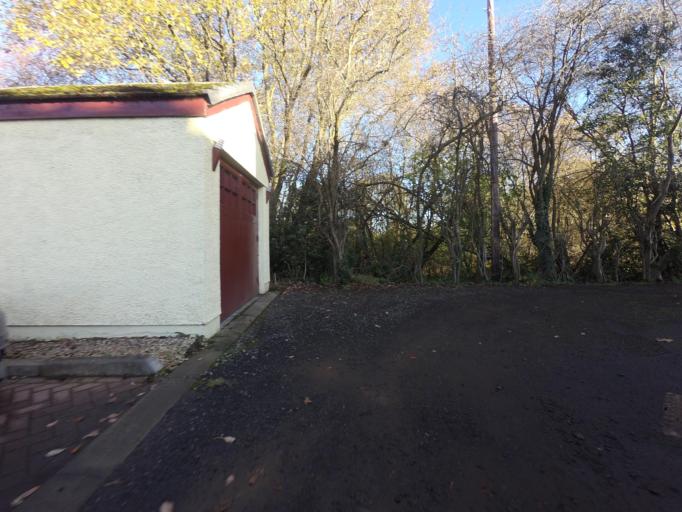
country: GB
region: Scotland
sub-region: West Lothian
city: Mid Calder
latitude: 55.9054
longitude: -3.4871
